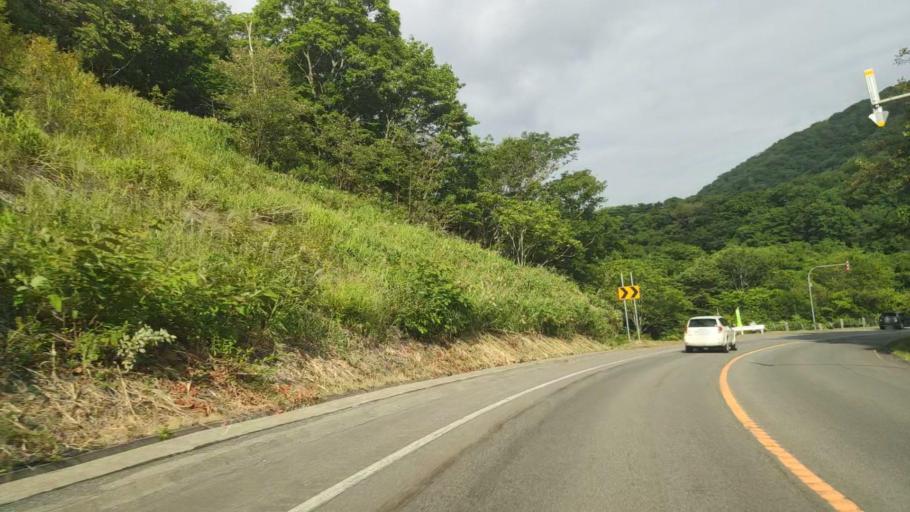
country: JP
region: Hokkaido
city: Ishikari
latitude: 43.4846
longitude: 141.3996
